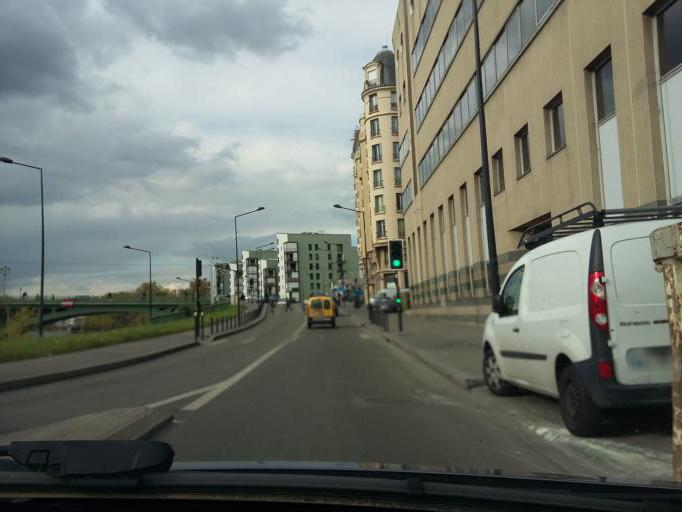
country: FR
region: Ile-de-France
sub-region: Departement de Seine-Saint-Denis
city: Villetaneuse
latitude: 48.9350
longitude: 2.3427
